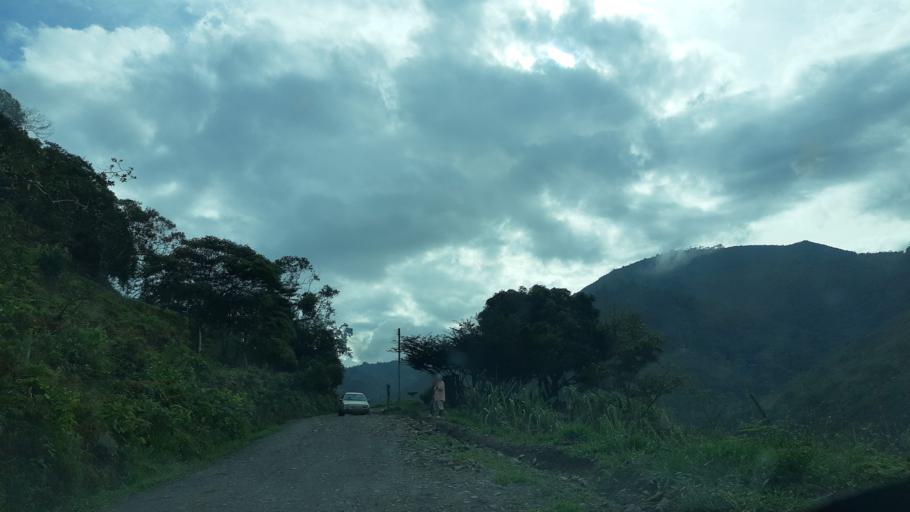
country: CO
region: Boyaca
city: Chivor
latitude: 4.9169
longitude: -73.3113
